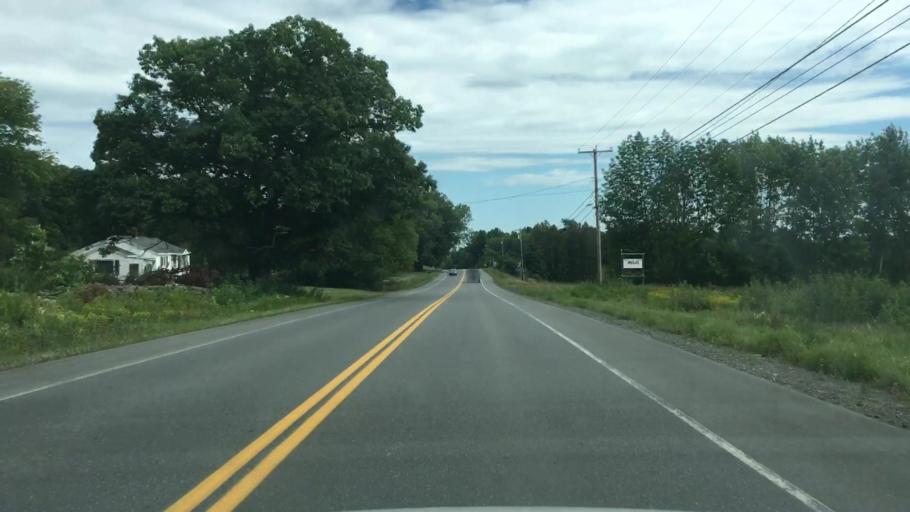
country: US
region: Maine
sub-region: Piscataquis County
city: Milo
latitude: 45.2441
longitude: -69.0124
